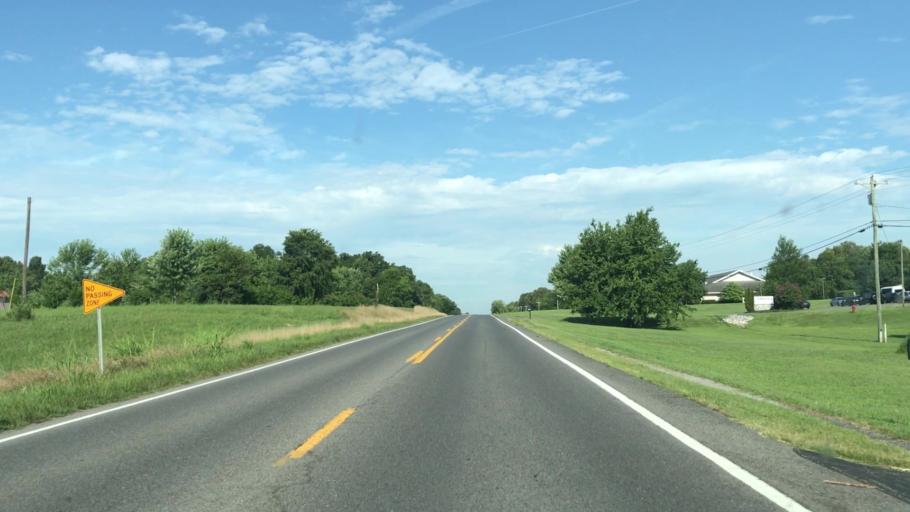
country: US
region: Kentucky
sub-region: Livingston County
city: Ledbetter
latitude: 37.0067
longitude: -88.4537
